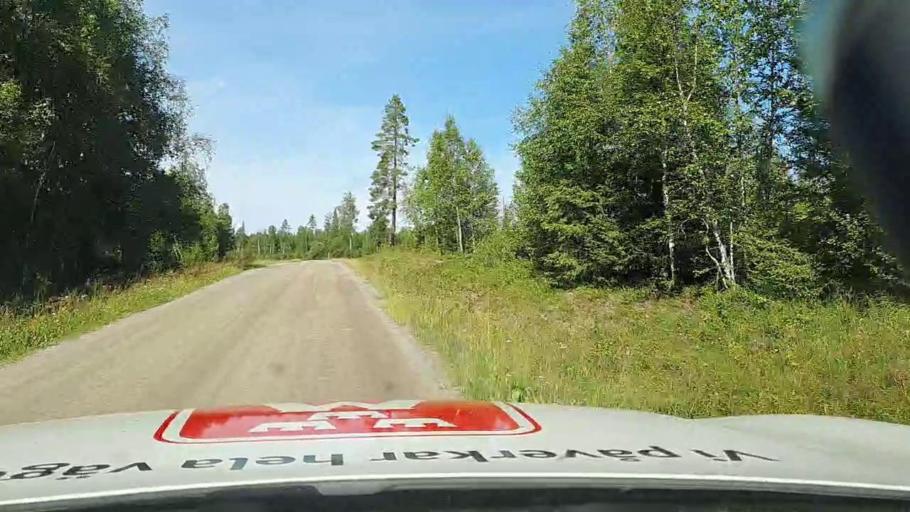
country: SE
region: Jaemtland
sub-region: Stroemsunds Kommun
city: Stroemsund
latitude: 63.7148
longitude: 15.2996
